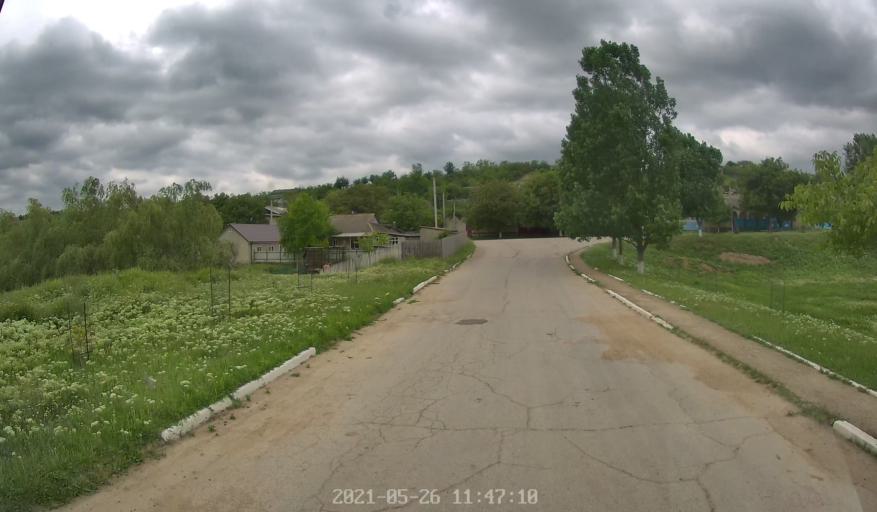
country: MD
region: Hincesti
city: Dancu
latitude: 46.7885
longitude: 28.3522
